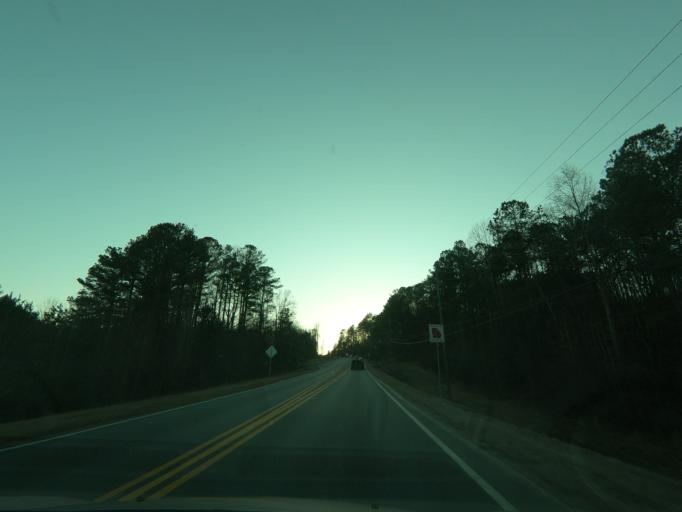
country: US
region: Georgia
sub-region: Cherokee County
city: Ball Ground
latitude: 34.2929
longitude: -84.2644
